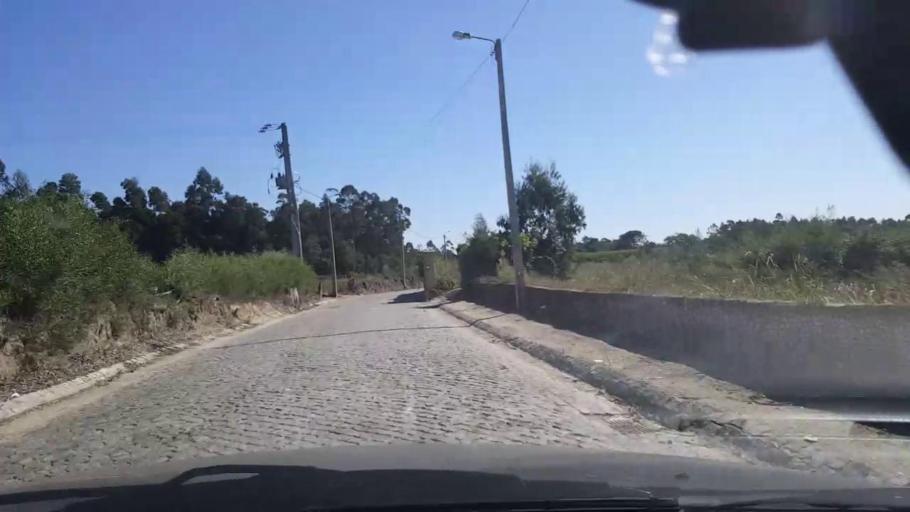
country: PT
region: Porto
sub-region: Vila do Conde
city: Arvore
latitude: 41.3155
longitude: -8.6884
